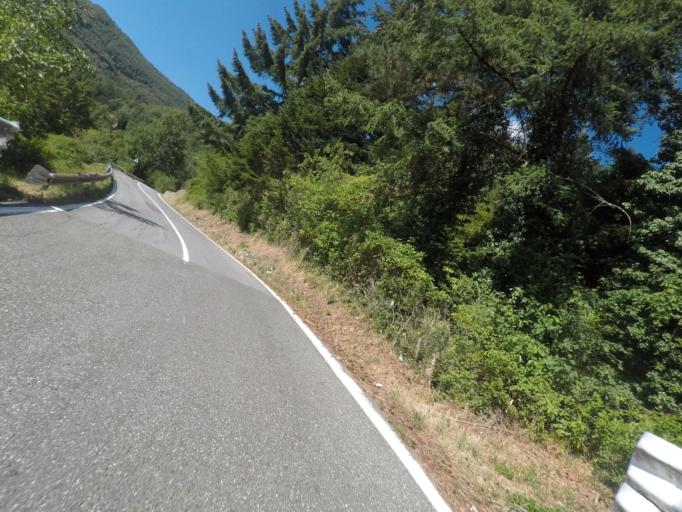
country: IT
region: Tuscany
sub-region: Provincia di Massa-Carrara
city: Fivizzano
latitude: 44.2542
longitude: 10.1751
